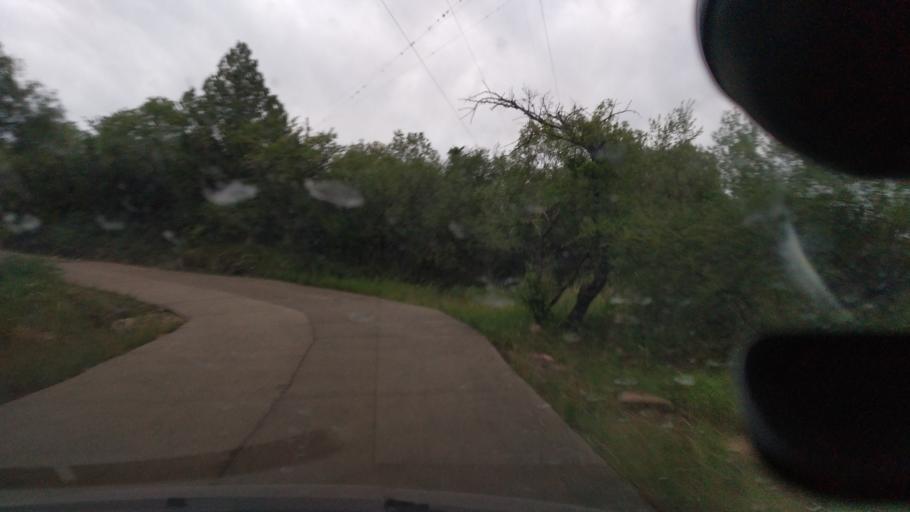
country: AR
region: Cordoba
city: Villa Las Rosas
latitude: -31.8780
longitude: -65.0235
